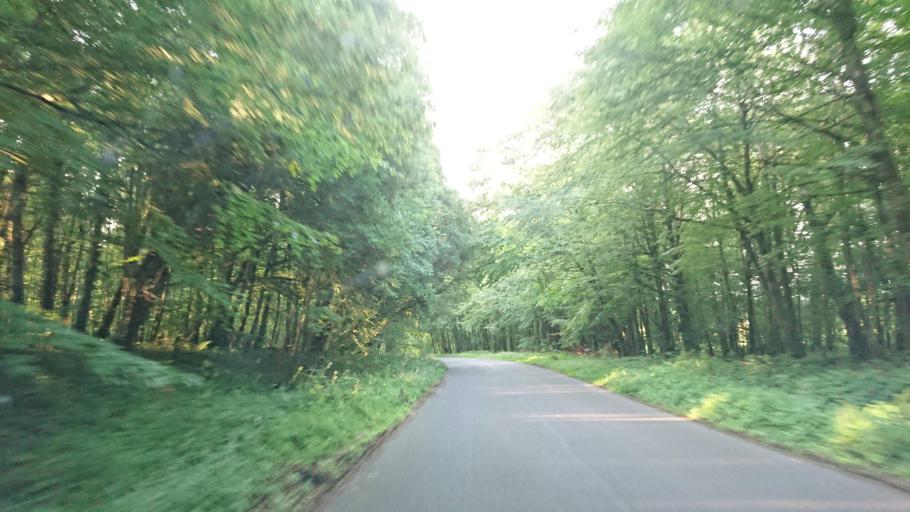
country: IE
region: Connaught
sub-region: Roscommon
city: Boyle
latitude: 53.9711
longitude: -8.2458
